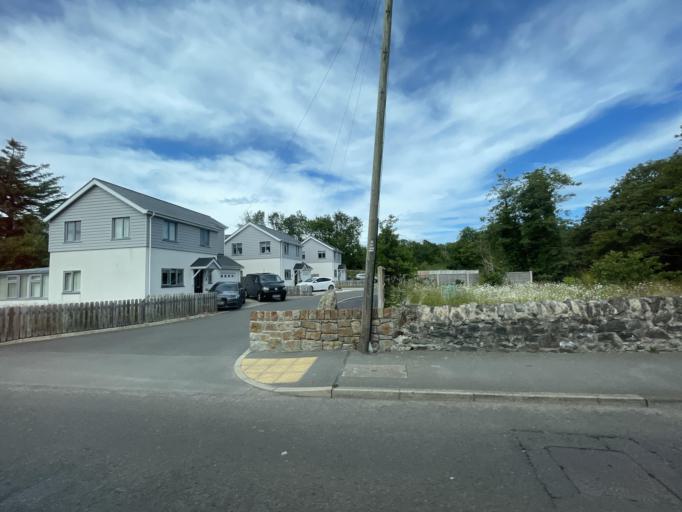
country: GB
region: Wales
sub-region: Anglesey
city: Llanfairpwllgwyngyll
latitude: 53.2218
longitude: -4.2147
